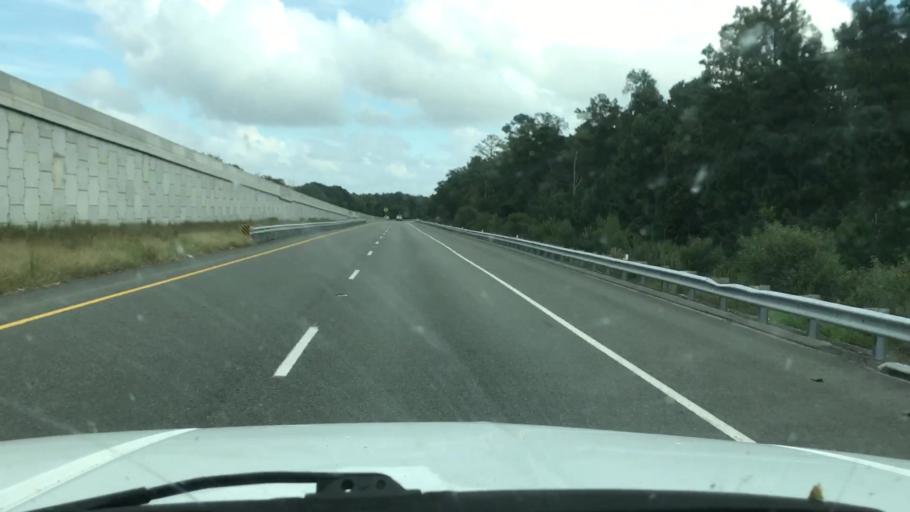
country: US
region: Virginia
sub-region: Henrico County
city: Short Pump
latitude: 37.6597
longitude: -77.6005
